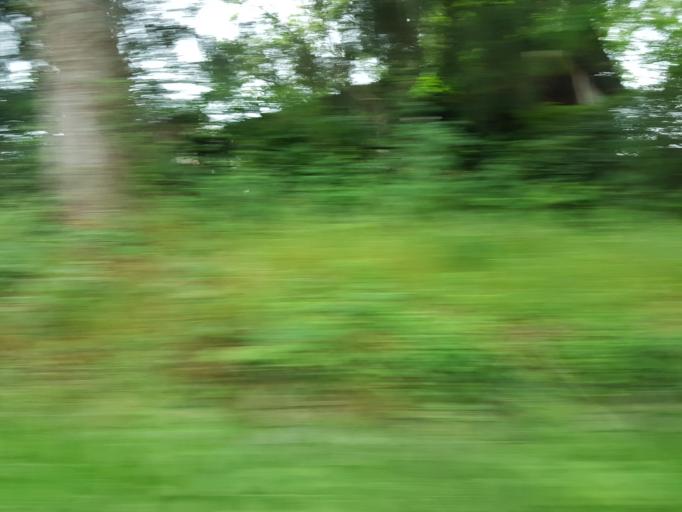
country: FR
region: Bourgogne
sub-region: Departement de la Nievre
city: Lormes
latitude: 47.1639
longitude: 3.8403
